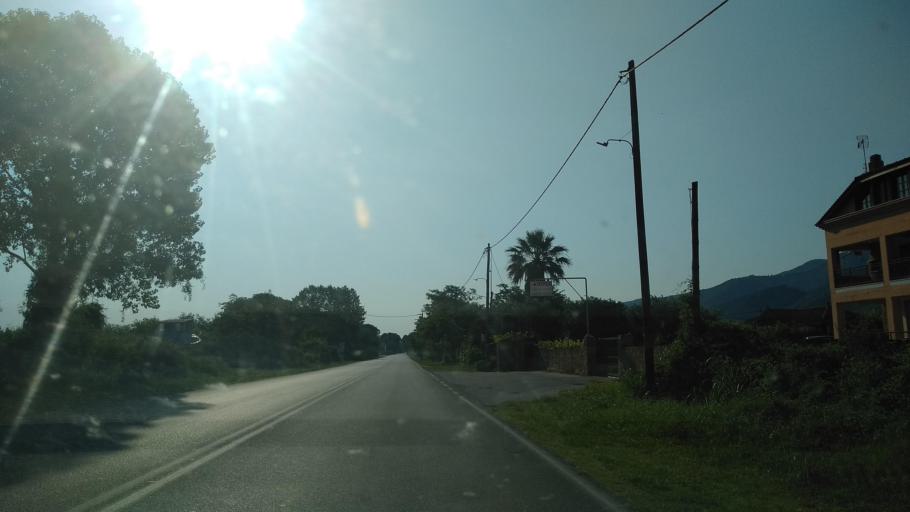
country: GR
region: Central Macedonia
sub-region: Nomos Thessalonikis
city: Stavros
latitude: 40.6693
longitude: 23.6709
